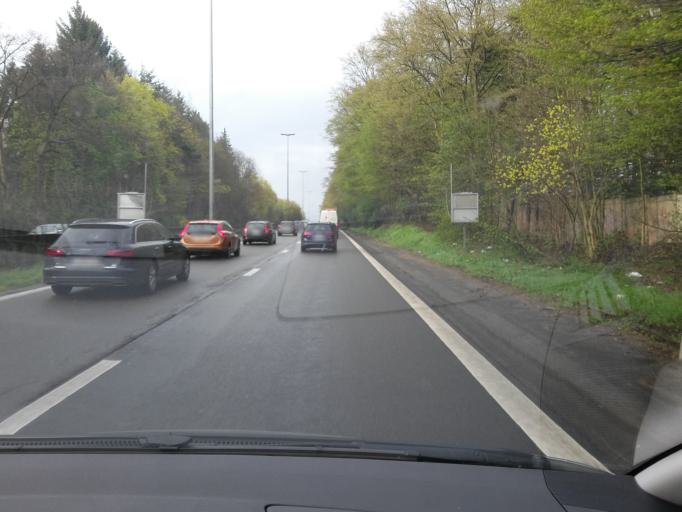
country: BE
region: Wallonia
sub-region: Province du Brabant Wallon
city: Waterloo
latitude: 50.7222
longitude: 4.4149
